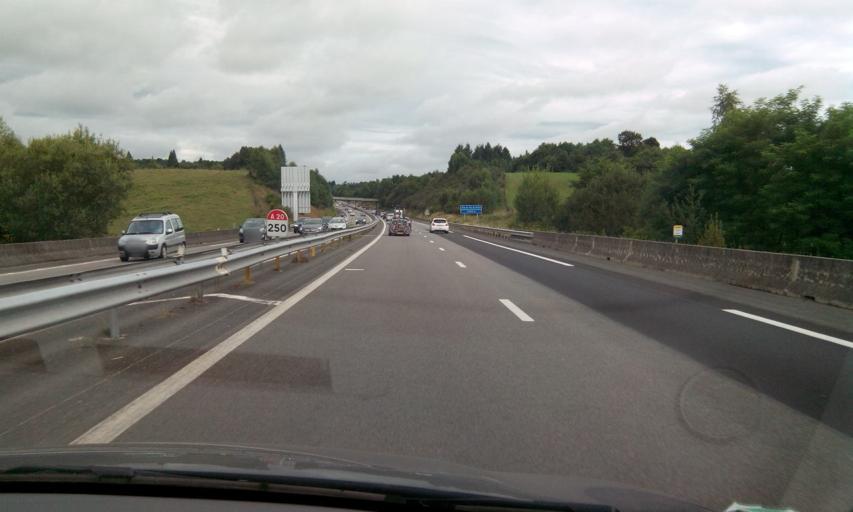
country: FR
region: Limousin
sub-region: Departement de la Correze
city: Vigeois
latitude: 45.3387
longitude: 1.5724
